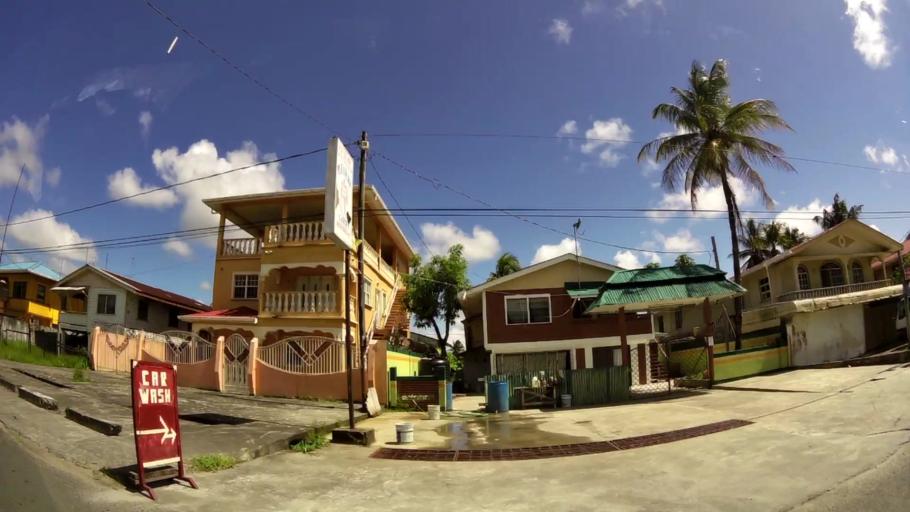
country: GY
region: Demerara-Mahaica
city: Georgetown
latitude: 6.7831
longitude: -58.1281
